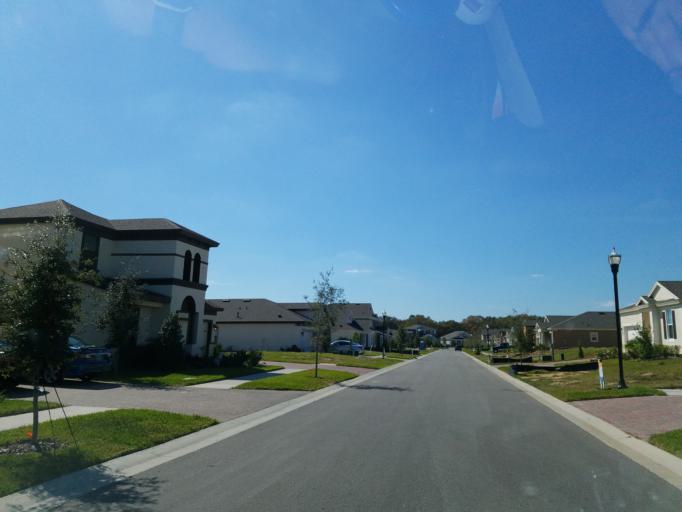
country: US
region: Florida
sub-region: Hillsborough County
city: Brandon
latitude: 27.9263
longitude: -82.2657
